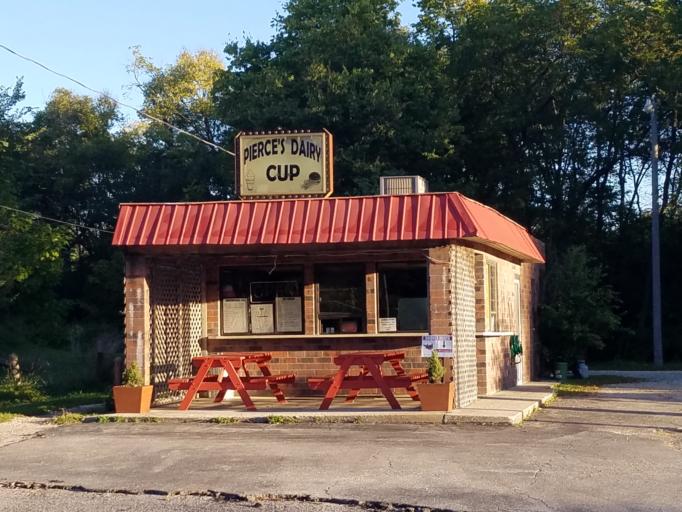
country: US
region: Iowa
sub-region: Decatur County
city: Lamoni
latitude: 40.6224
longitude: -93.9393
